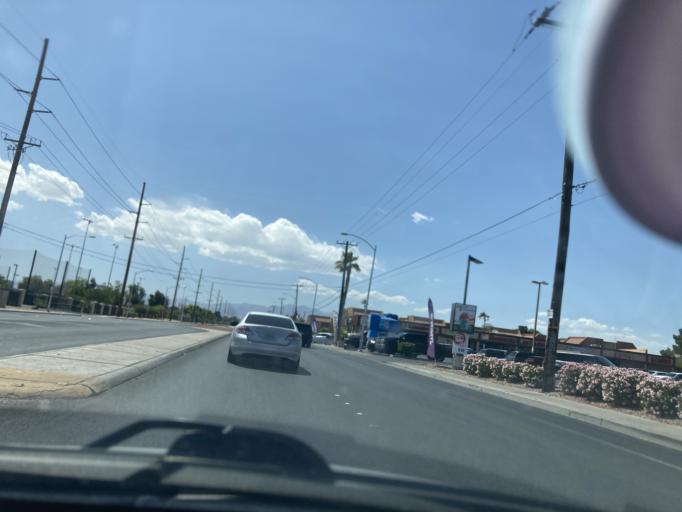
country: US
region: Nevada
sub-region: Clark County
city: North Las Vegas
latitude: 36.1810
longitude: -115.0987
